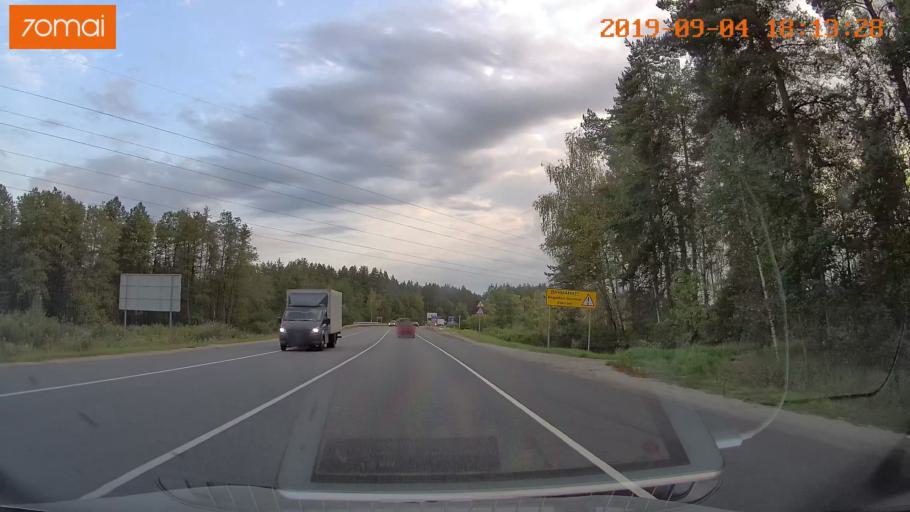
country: RU
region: Moskovskaya
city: Lopatinskiy
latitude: 55.3599
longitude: 38.7344
